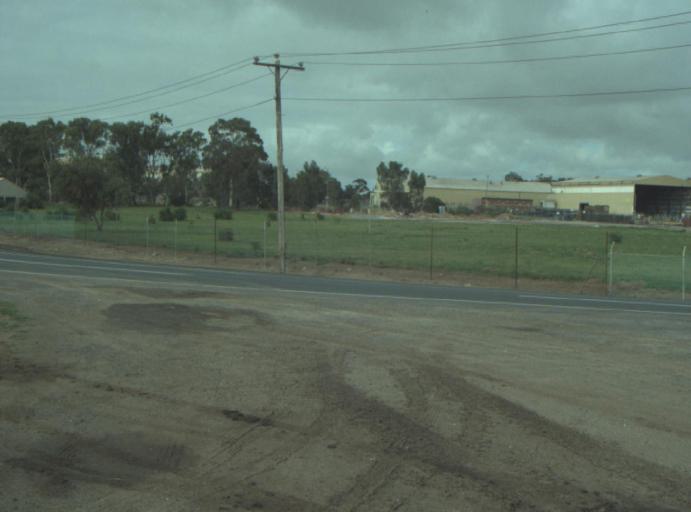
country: AU
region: Victoria
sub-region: Greater Geelong
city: Bell Park
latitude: -38.0799
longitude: 144.3857
